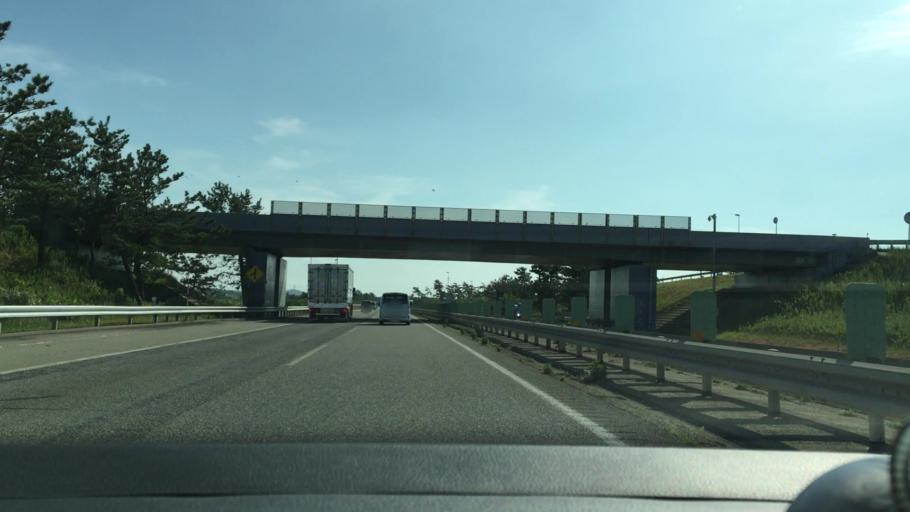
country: JP
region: Ishikawa
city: Komatsu
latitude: 36.3727
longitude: 136.3595
